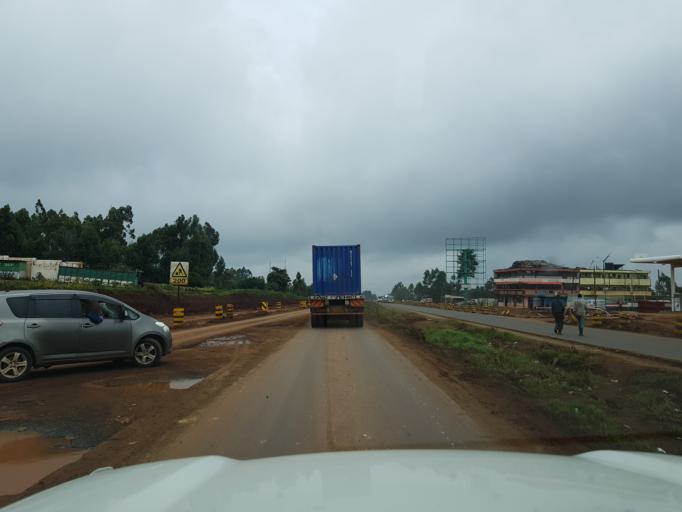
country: KE
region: Kiambu
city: Limuru
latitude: -1.1351
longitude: 36.6355
